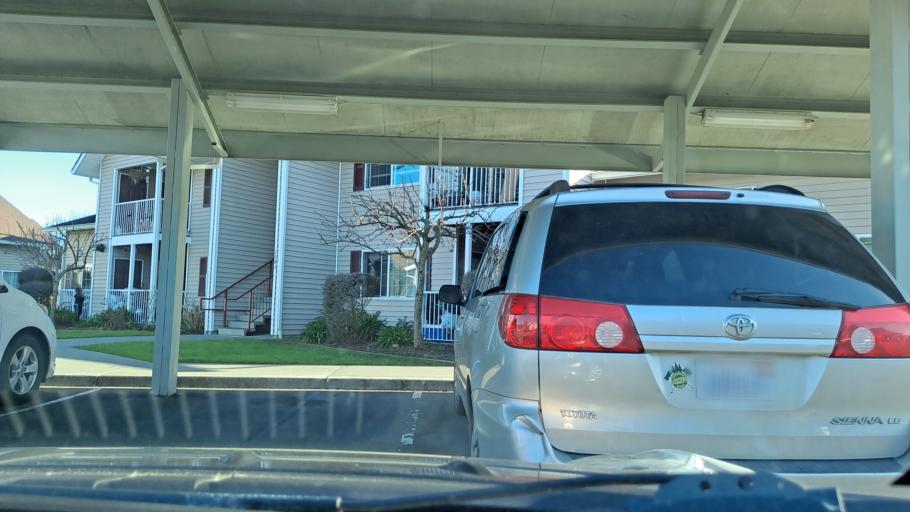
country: US
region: California
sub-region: Humboldt County
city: Fortuna
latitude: 40.5936
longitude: -124.1440
